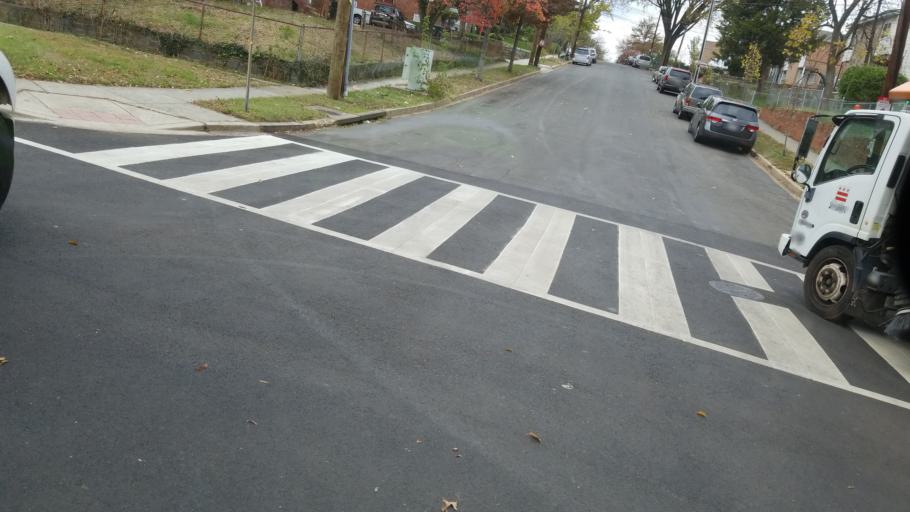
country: US
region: Maryland
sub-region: Prince George's County
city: Capitol Heights
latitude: 38.8917
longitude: -76.9258
